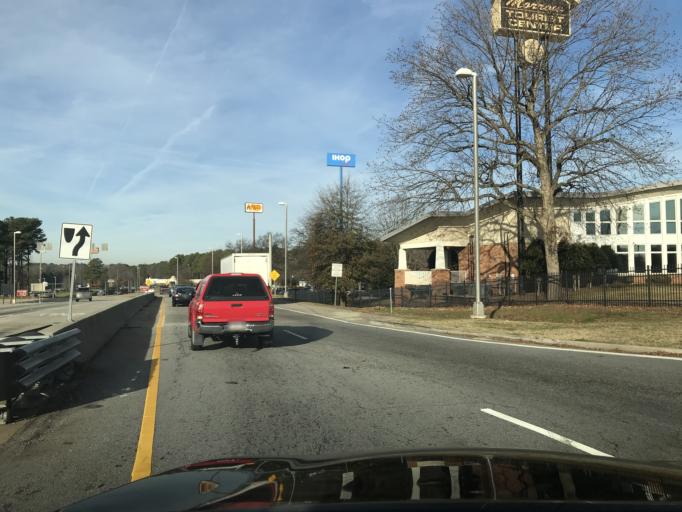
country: US
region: Georgia
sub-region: Clayton County
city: Morrow
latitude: 33.5781
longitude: -84.3410
